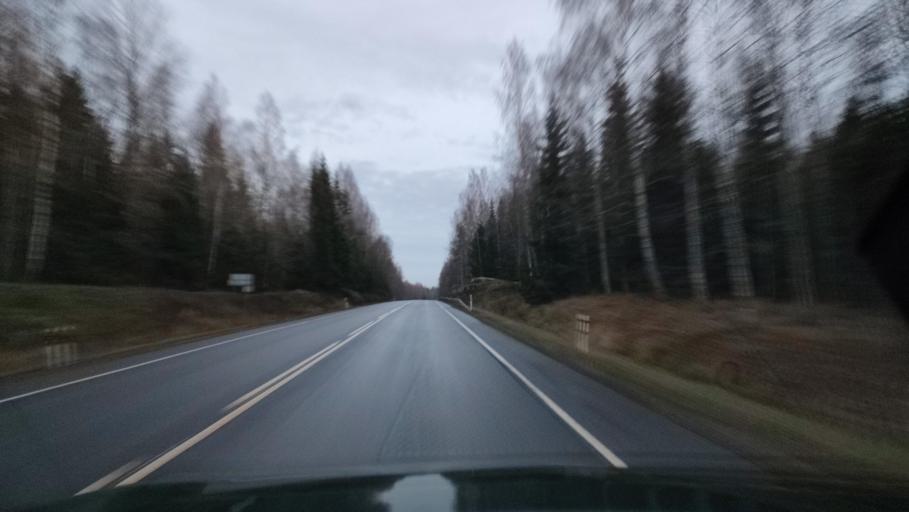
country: FI
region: Ostrobothnia
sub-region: Vaasa
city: Ristinummi
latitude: 62.9847
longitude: 21.7680
